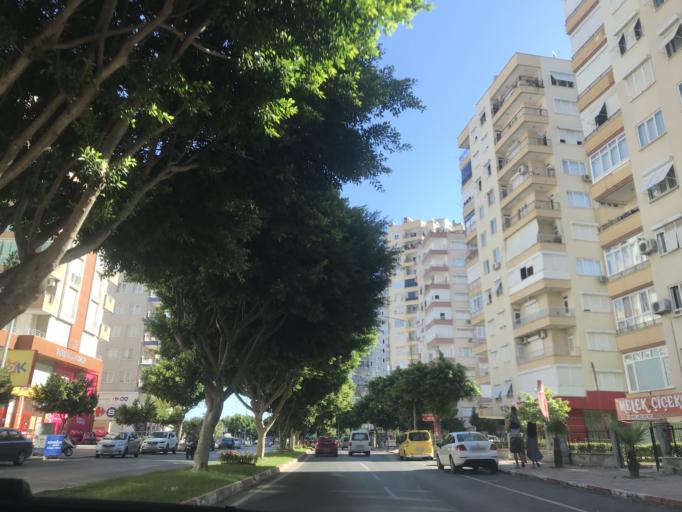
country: TR
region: Antalya
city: Antalya
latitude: 36.8977
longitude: 30.6299
